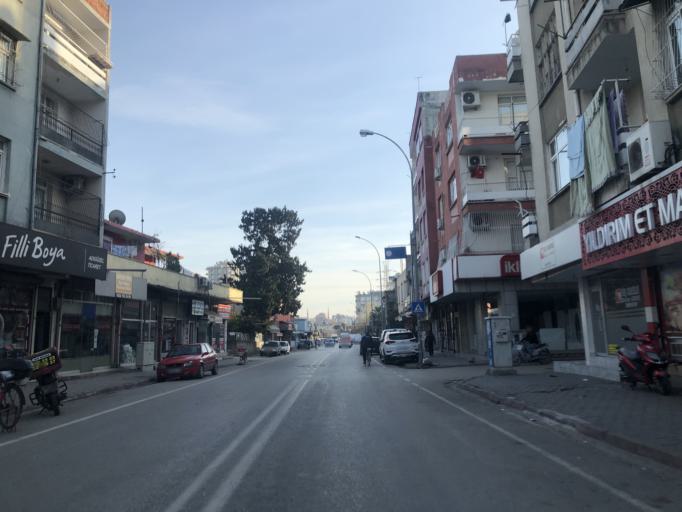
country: TR
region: Adana
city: Adana
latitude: 37.0124
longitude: 35.3148
